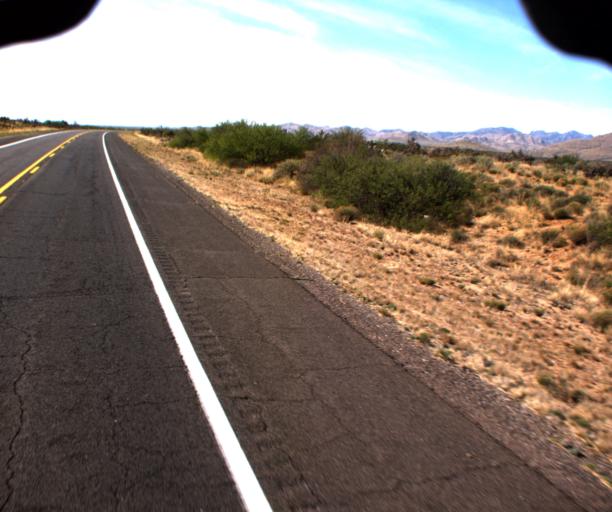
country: US
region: Arizona
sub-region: Graham County
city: Swift Trail Junction
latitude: 32.6271
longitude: -109.6902
